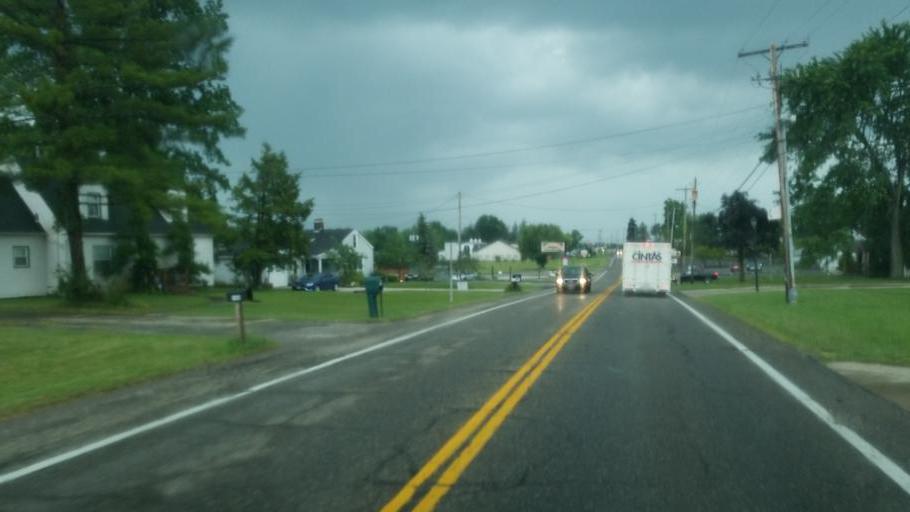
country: US
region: Ohio
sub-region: Trumbull County
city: Champion Heights
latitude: 41.2886
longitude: -80.8472
